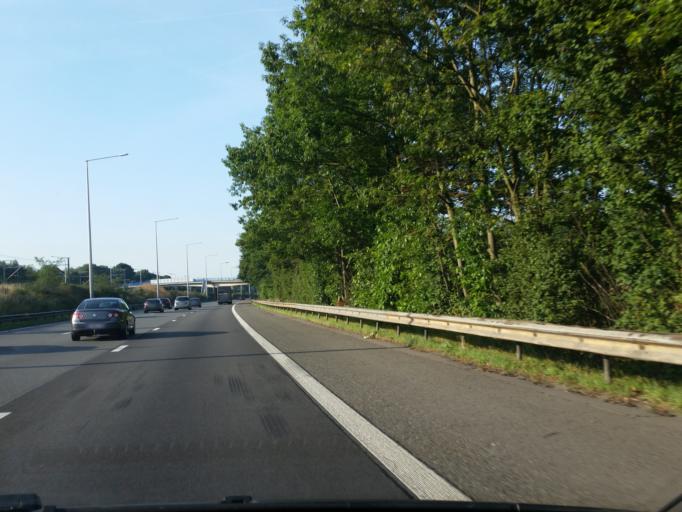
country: BE
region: Flanders
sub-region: Provincie Vlaams-Brabant
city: Zemst
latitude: 50.9670
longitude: 4.4905
